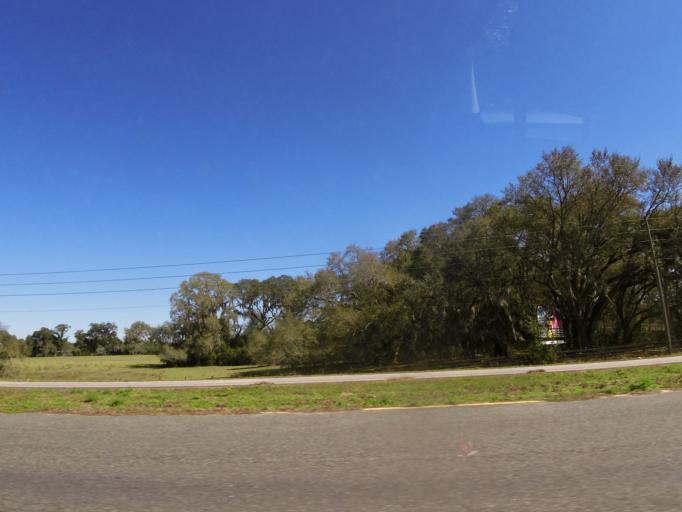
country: US
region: Florida
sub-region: Orange County
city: Tangerine
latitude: 28.7828
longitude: -81.6247
